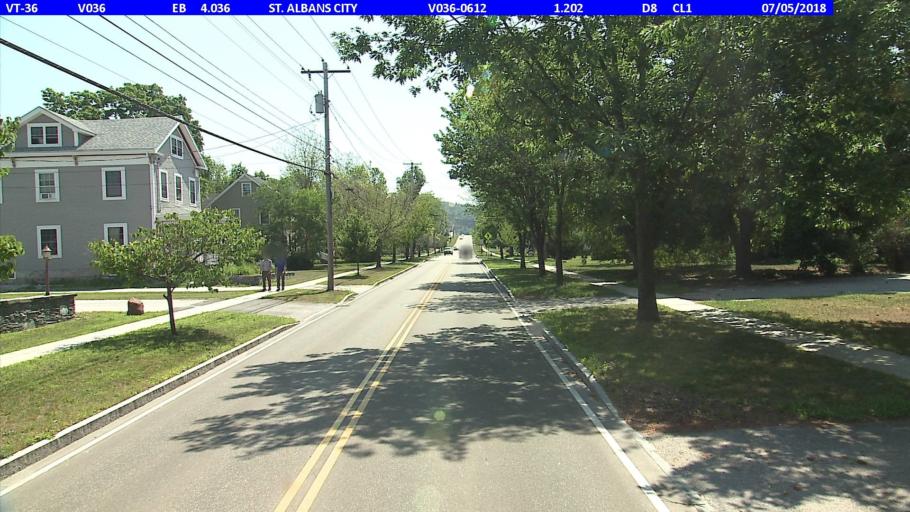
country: US
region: Vermont
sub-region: Franklin County
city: Saint Albans
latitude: 44.8083
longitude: -73.0773
